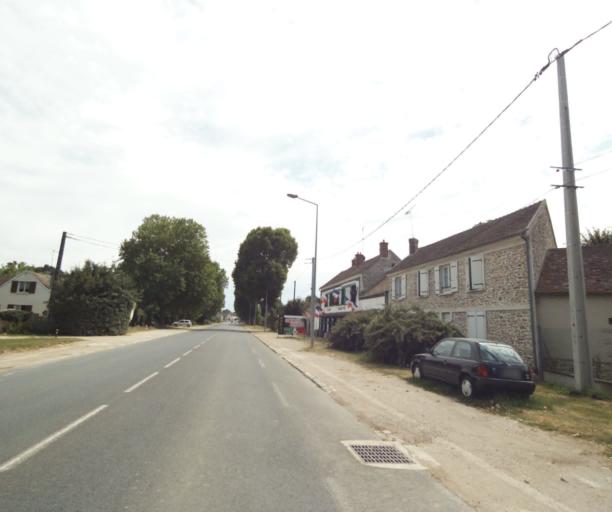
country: FR
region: Ile-de-France
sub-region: Departement de Seine-et-Marne
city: Chailly-en-Biere
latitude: 48.4703
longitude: 2.6037
